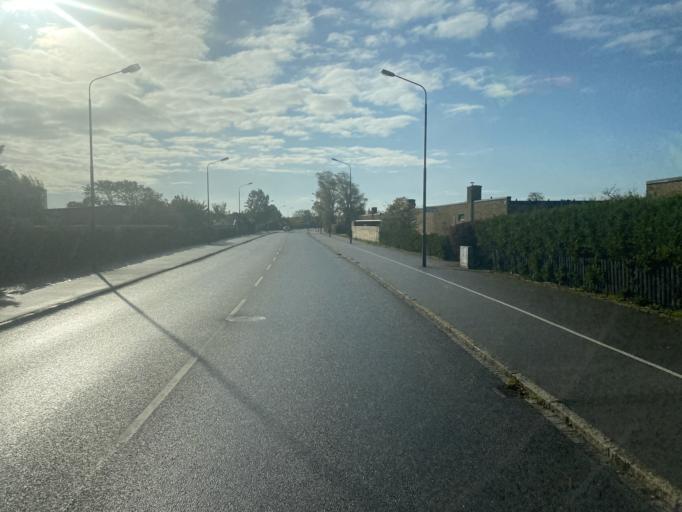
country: SE
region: Skane
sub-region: Malmo
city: Bunkeflostrand
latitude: 55.5774
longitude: 12.9638
